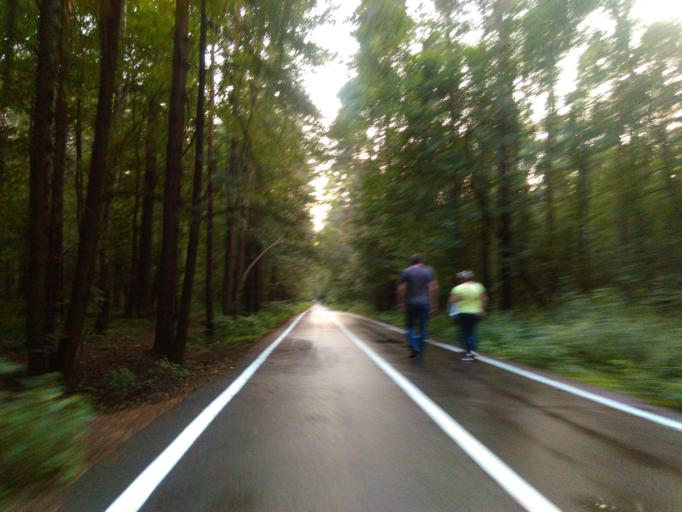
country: RU
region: Moscow
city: Babushkin
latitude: 55.8655
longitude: 37.7227
